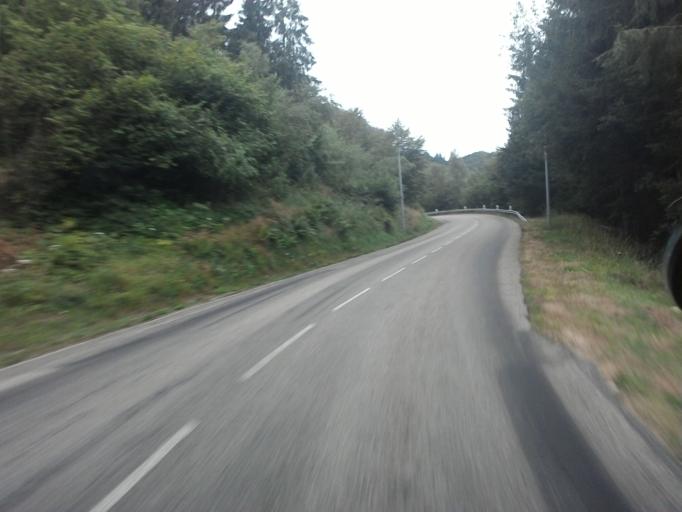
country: FR
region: Lorraine
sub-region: Departement des Vosges
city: Le Thillot
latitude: 47.8613
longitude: 6.7518
